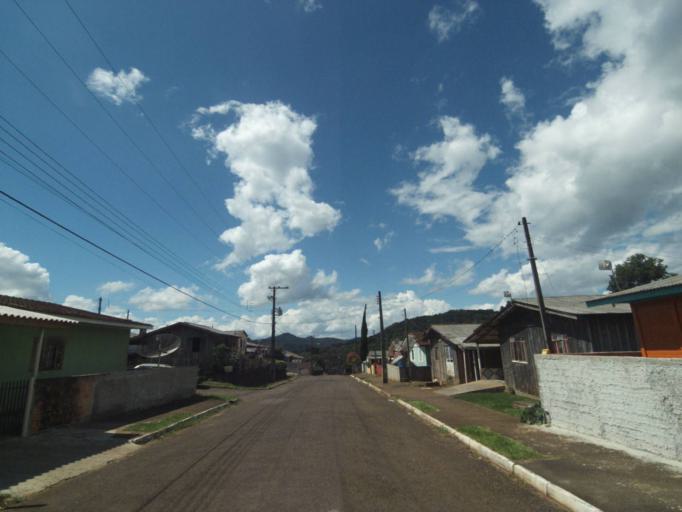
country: BR
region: Parana
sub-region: Uniao Da Vitoria
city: Uniao da Vitoria
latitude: -26.1729
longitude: -51.5514
